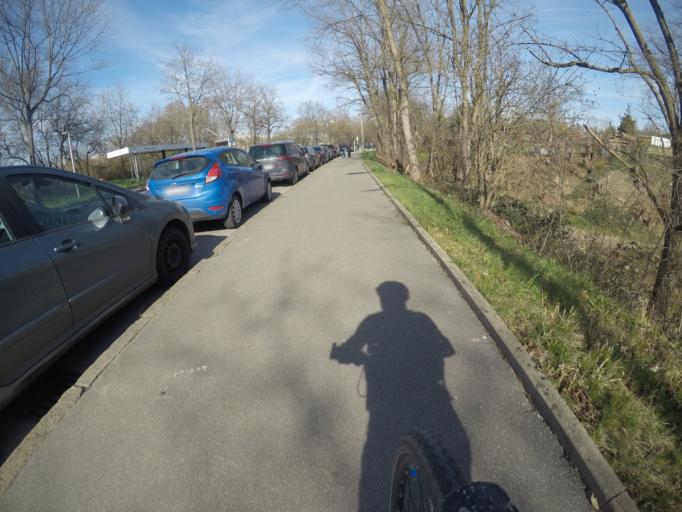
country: DE
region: Baden-Wuerttemberg
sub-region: Regierungsbezirk Stuttgart
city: Stuttgart Muehlhausen
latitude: 48.8291
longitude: 9.2120
